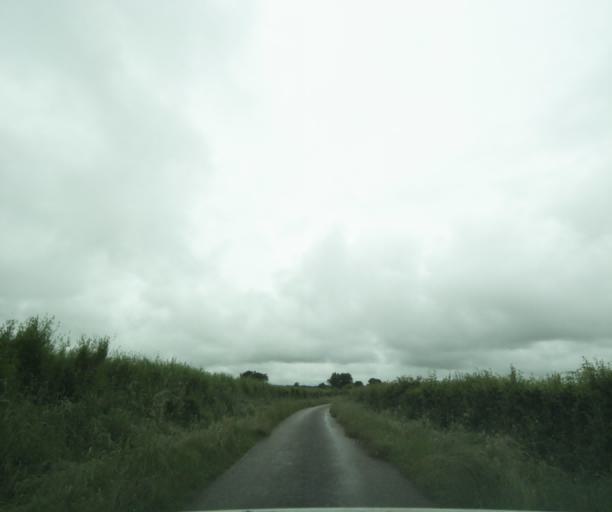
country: FR
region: Bourgogne
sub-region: Departement de Saone-et-Loire
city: Charolles
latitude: 46.4532
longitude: 4.3255
